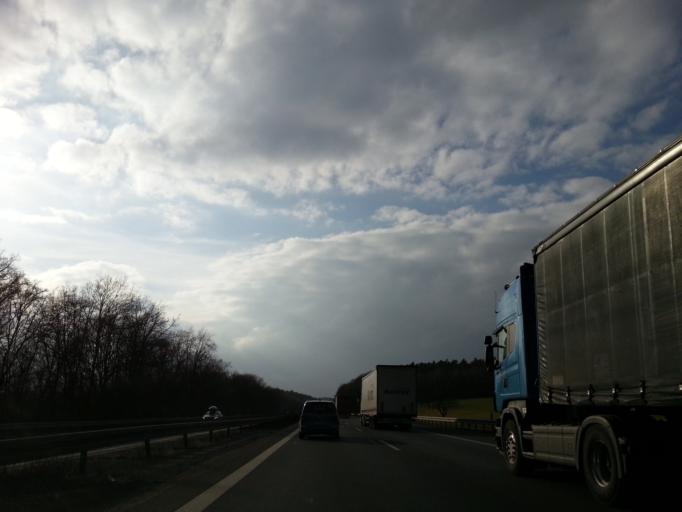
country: DE
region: Bavaria
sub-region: Regierungsbezirk Mittelfranken
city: Wachenroth
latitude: 49.7314
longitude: 10.6898
